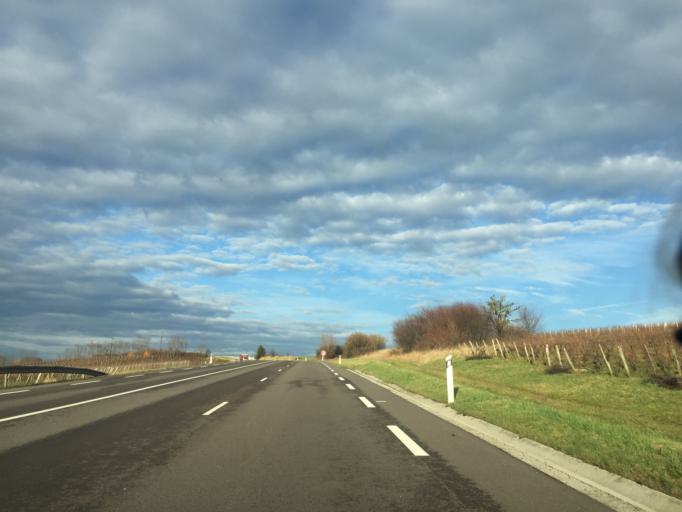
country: FR
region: Franche-Comte
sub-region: Departement du Jura
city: Arbois
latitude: 46.9260
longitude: 5.7751
